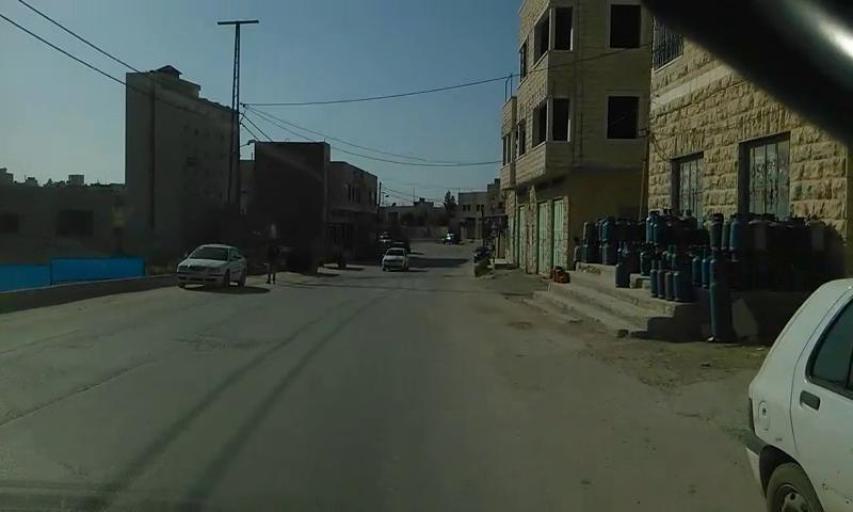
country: PS
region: West Bank
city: Yuta
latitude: 31.4518
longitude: 35.0969
